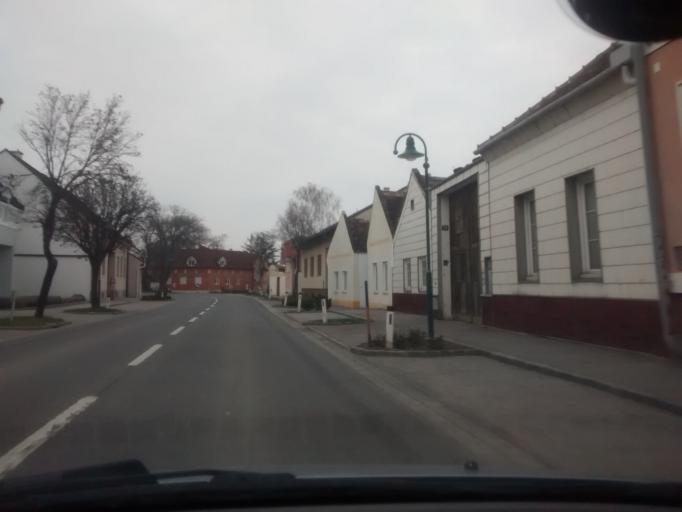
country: AT
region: Lower Austria
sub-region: Politischer Bezirk Modling
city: Munchendorf
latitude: 48.0317
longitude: 16.3808
